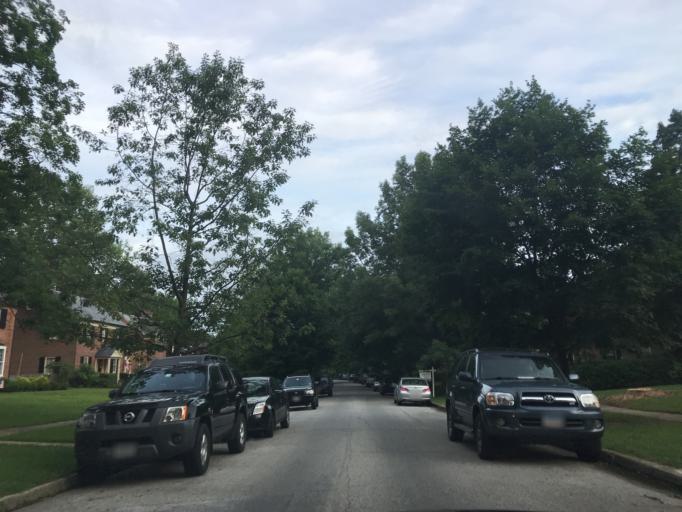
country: US
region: Maryland
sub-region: Baltimore County
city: Towson
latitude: 39.3626
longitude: -76.6174
